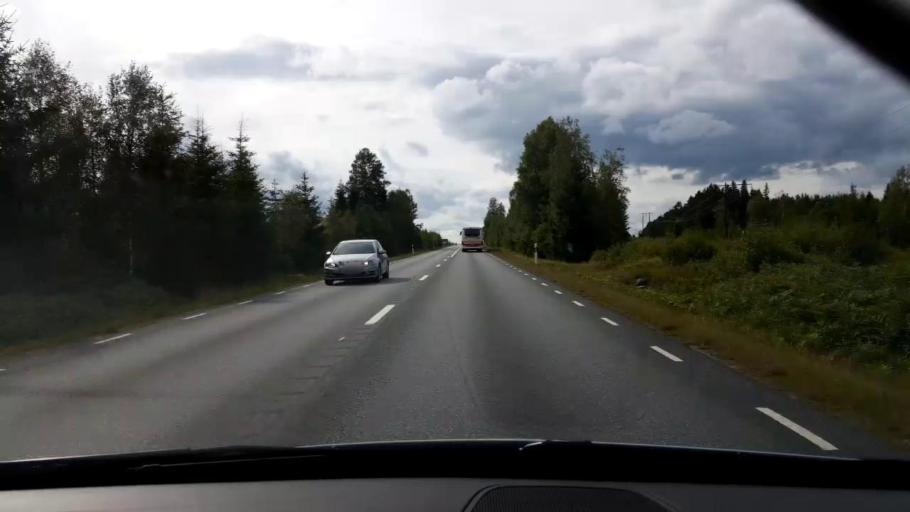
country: SE
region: Joenkoeping
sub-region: Savsjo Kommun
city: Saevsjoe
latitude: 57.3926
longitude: 14.7270
